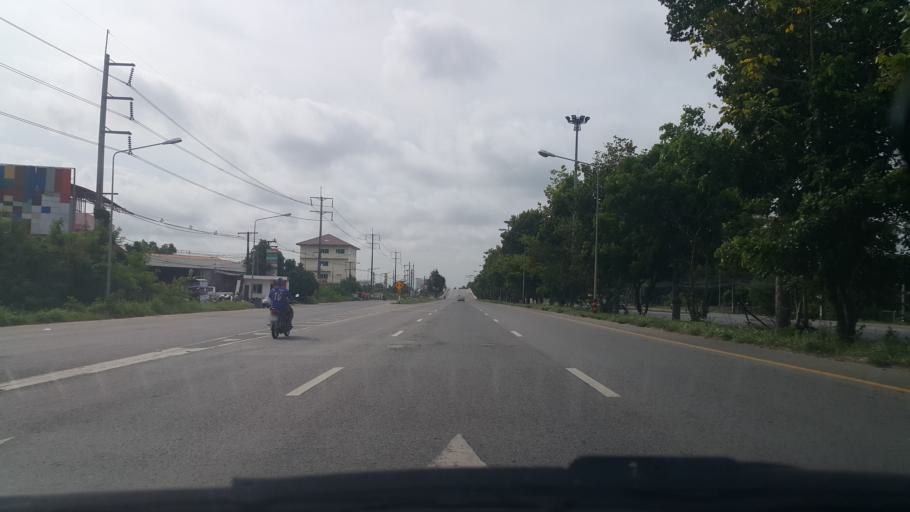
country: TH
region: Rayong
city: Rayong
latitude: 12.6791
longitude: 101.3016
